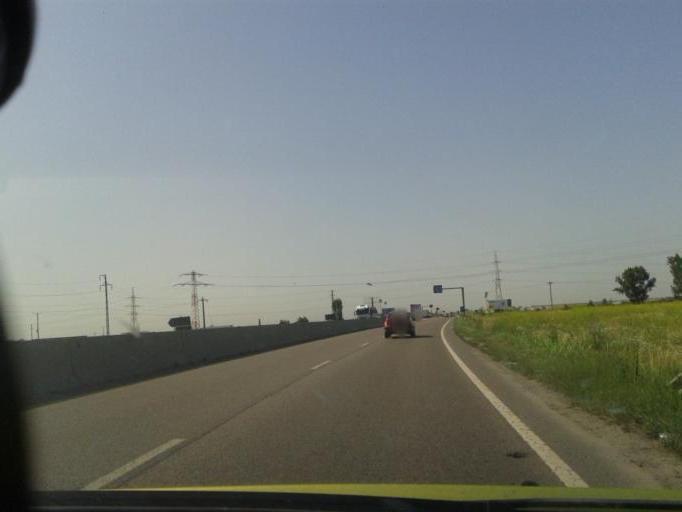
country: RO
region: Prahova
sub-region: Comuna Paulesti
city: Paulesti
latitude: 44.9622
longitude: 25.9647
